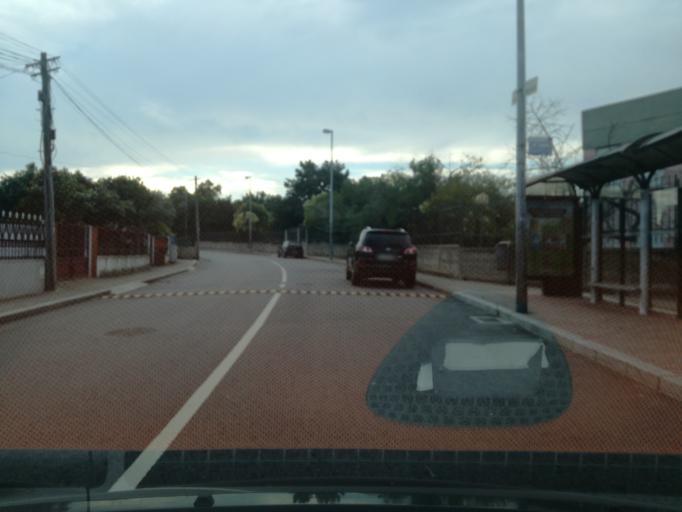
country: PT
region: Porto
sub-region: Maia
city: Anta
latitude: 41.2588
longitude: -8.6129
